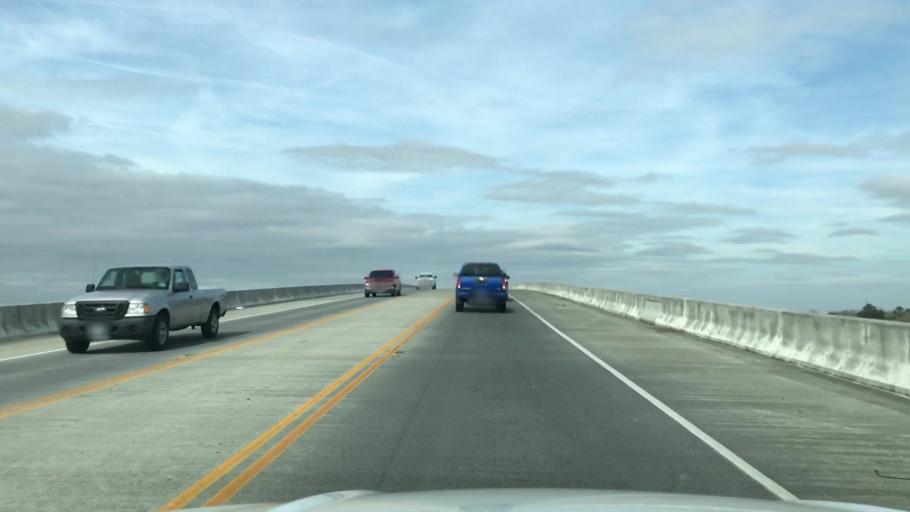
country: US
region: South Carolina
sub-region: Charleston County
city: Shell Point
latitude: 32.7834
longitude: -80.1066
